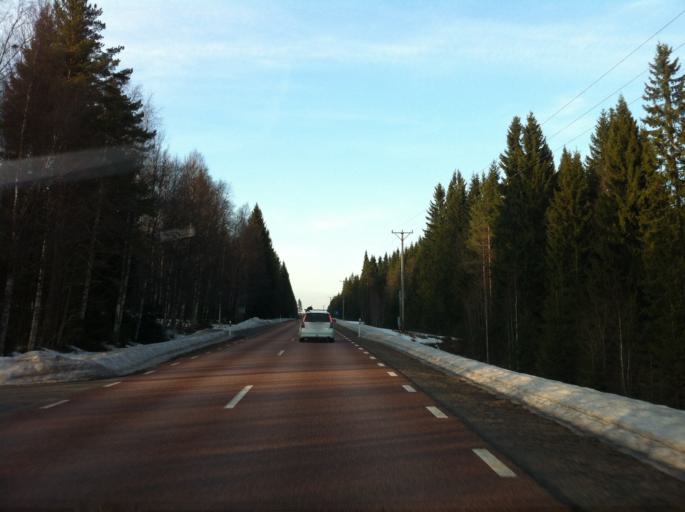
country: SE
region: Vaermland
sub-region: Filipstads Kommun
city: Lesjofors
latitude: 60.2100
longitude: 14.1875
